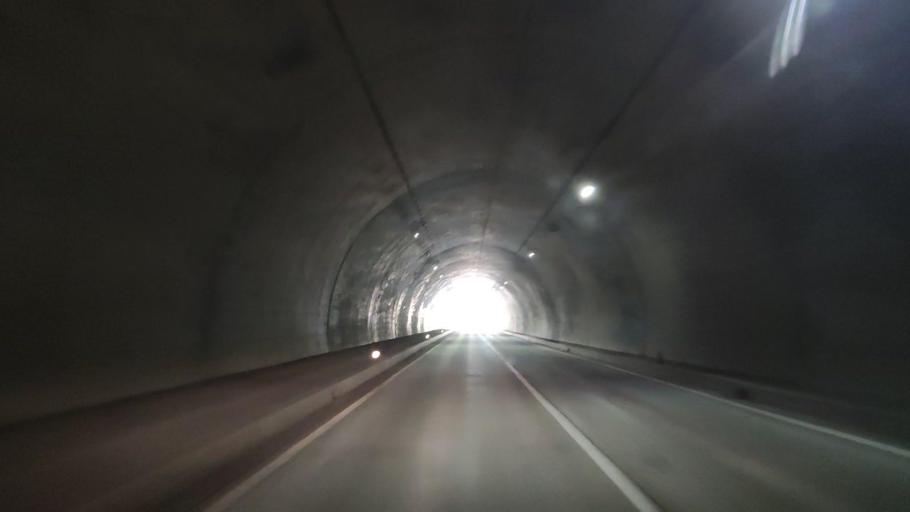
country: JP
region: Gifu
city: Takayama
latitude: 36.3357
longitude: 137.3011
